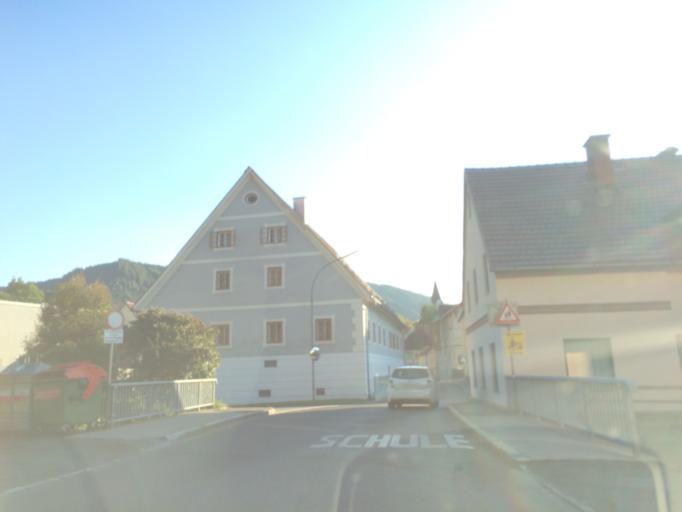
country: AT
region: Styria
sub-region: Politischer Bezirk Leoben
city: Leoben
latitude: 47.3661
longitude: 15.0983
